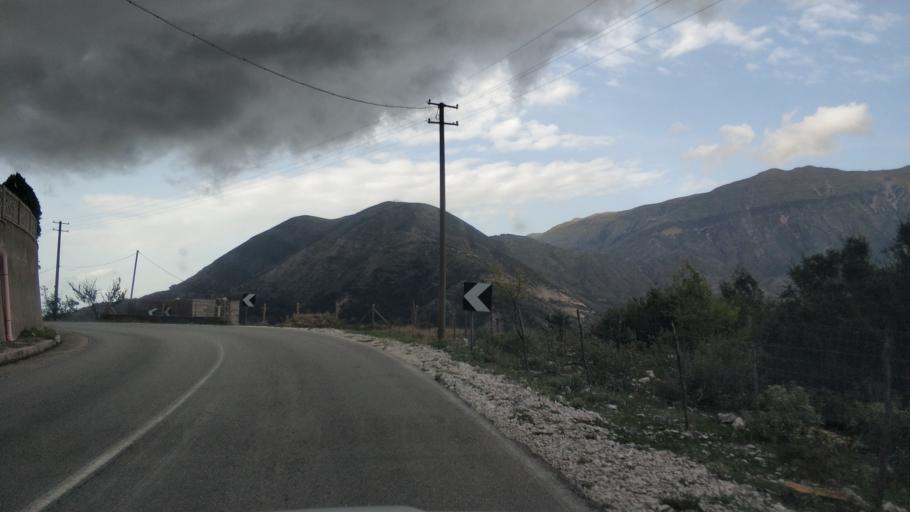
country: AL
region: Vlore
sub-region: Rrethi i Vlores
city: Brataj
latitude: 40.2362
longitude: 19.5551
